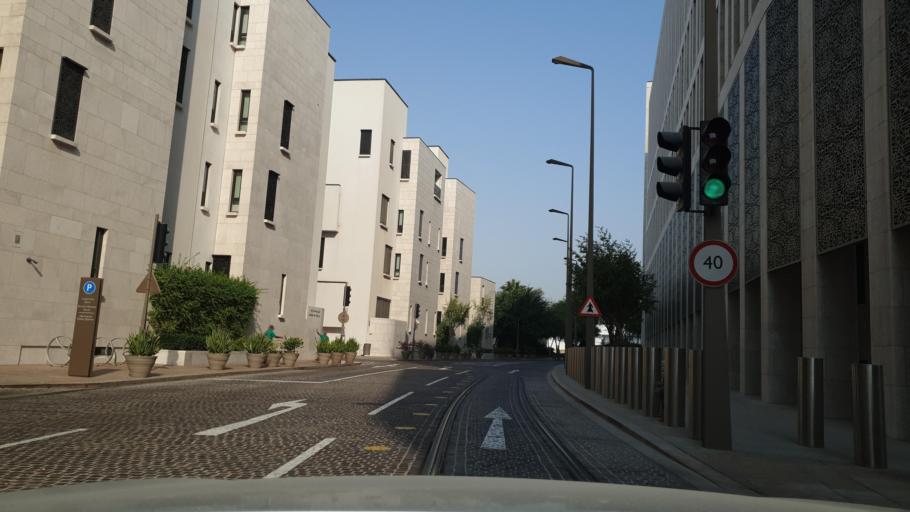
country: QA
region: Baladiyat ad Dawhah
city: Doha
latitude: 25.2870
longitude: 51.5270
